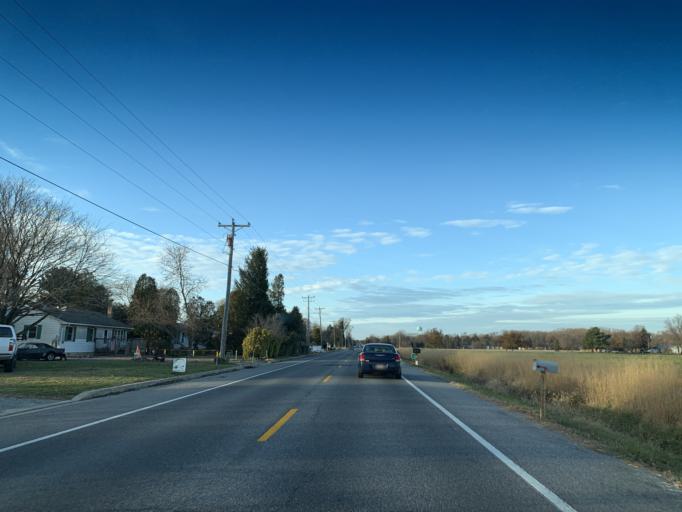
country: US
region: Maryland
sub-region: Kent County
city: Chestertown
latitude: 39.2666
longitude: -76.0883
